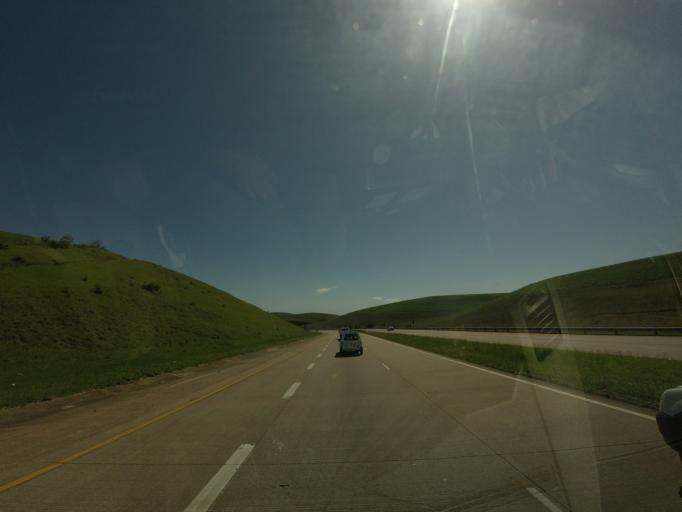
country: ZA
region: KwaZulu-Natal
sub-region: iLembe District Municipality
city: Stanger
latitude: -29.3891
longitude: 31.2958
